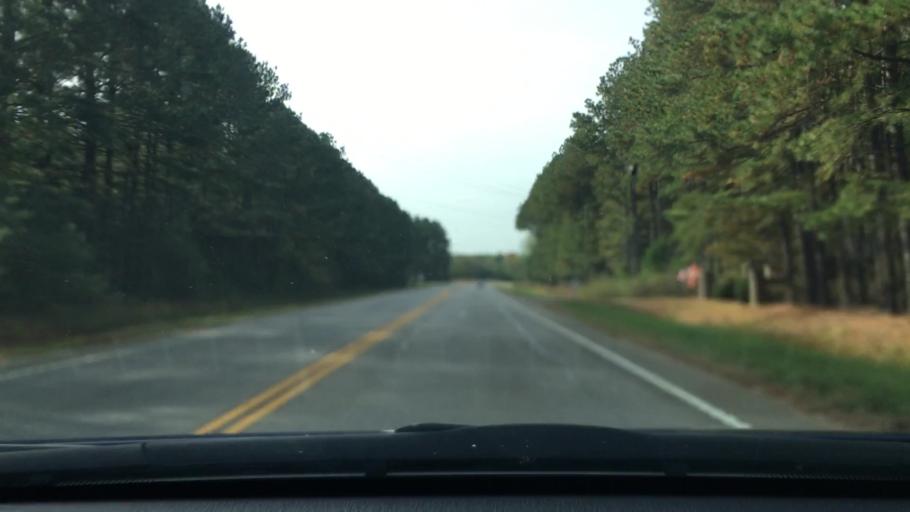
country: US
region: South Carolina
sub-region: Sumter County
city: Cherryvale
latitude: 33.9369
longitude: -80.4392
